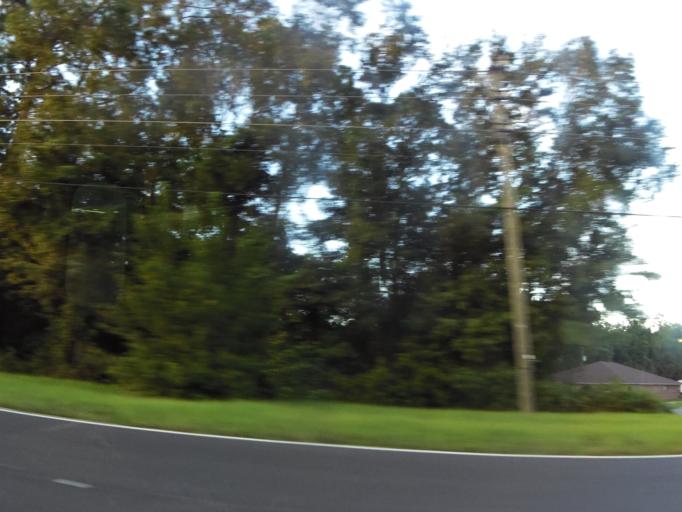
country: US
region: Georgia
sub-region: Camden County
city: Kingsland
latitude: 30.8008
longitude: -81.6808
